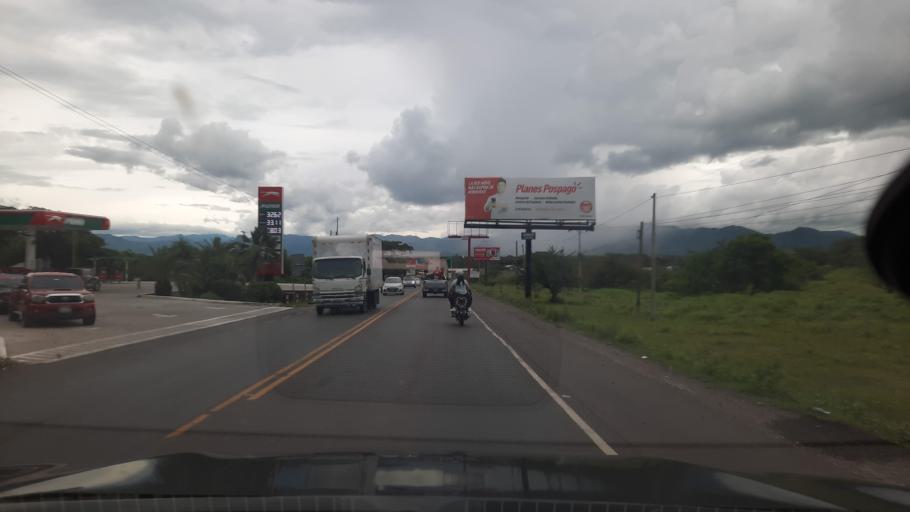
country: HN
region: Choluteca
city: Ciudad Choluteca
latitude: 13.3238
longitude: -87.2153
